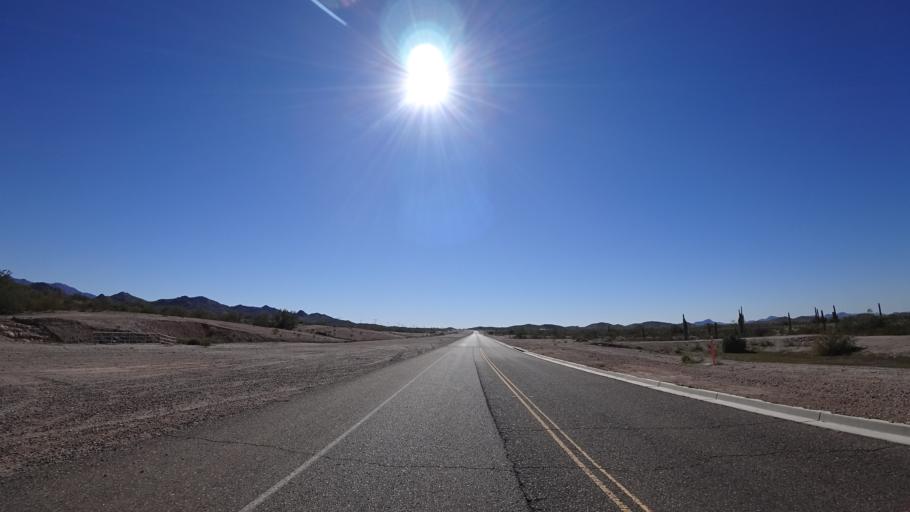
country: US
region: Arizona
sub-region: Maricopa County
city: Goodyear
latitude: 33.3760
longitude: -112.4202
